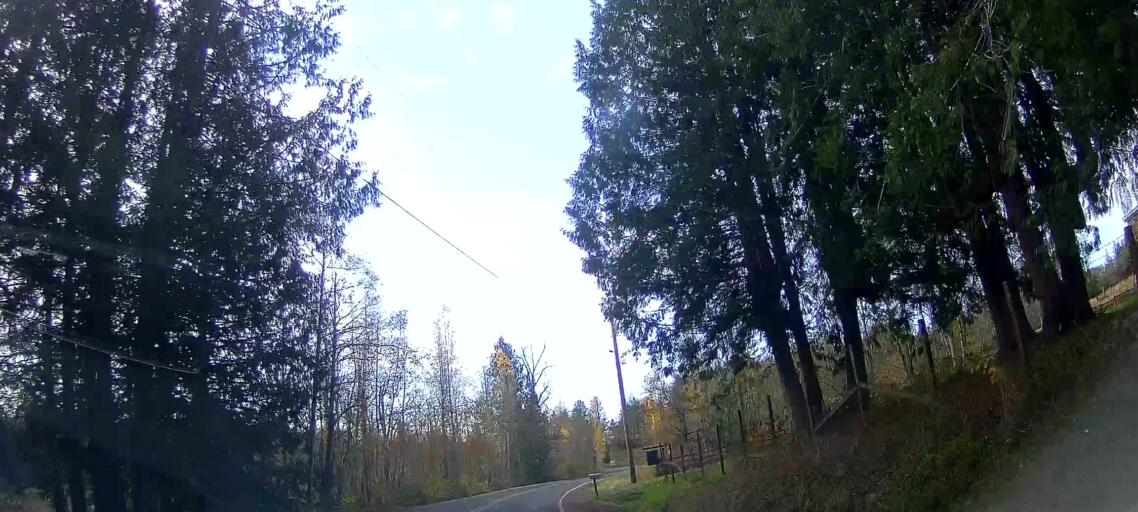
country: US
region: Washington
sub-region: Skagit County
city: Big Lake
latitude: 48.4124
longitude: -122.2100
